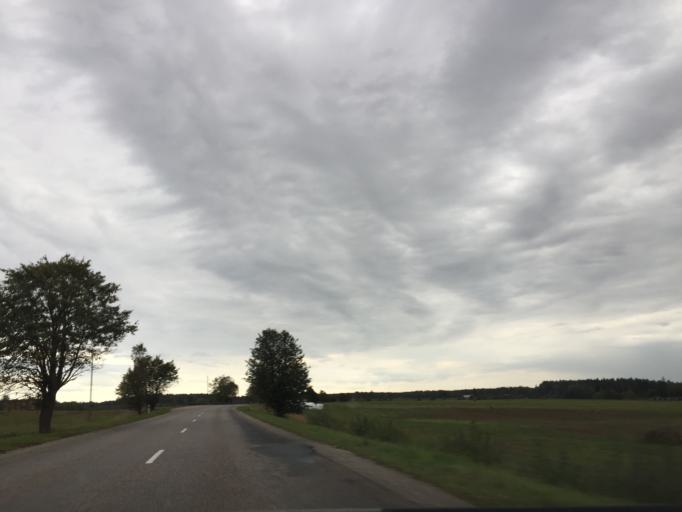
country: LV
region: Krimulda
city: Ragana
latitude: 57.2292
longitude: 24.6887
